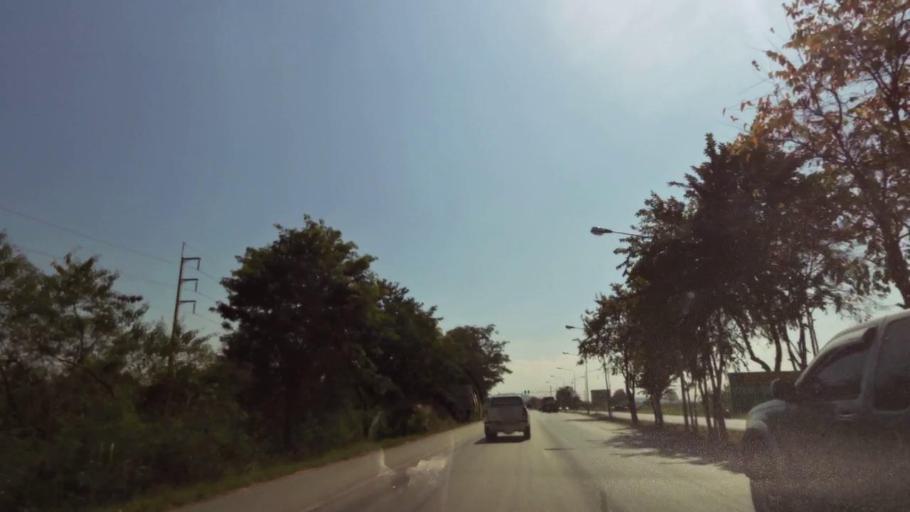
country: TH
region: Nakhon Sawan
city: Nakhon Sawan
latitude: 15.7698
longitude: 100.1214
